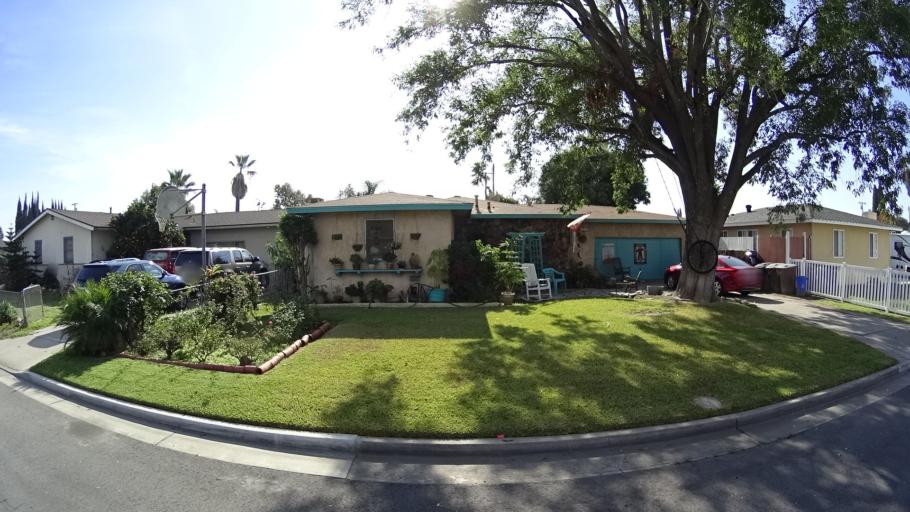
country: US
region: California
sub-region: Orange County
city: Garden Grove
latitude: 33.7901
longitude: -117.9286
